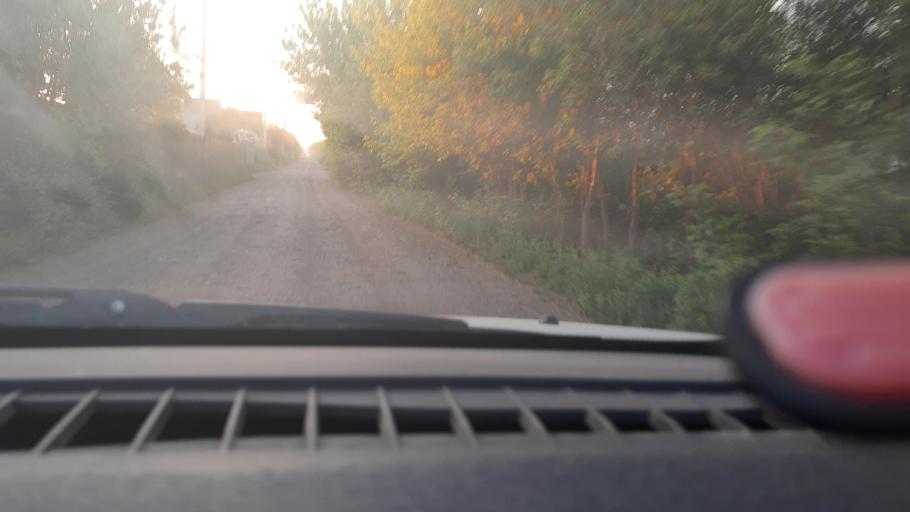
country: RU
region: Bashkortostan
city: Ufa
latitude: 54.5522
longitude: 55.9312
